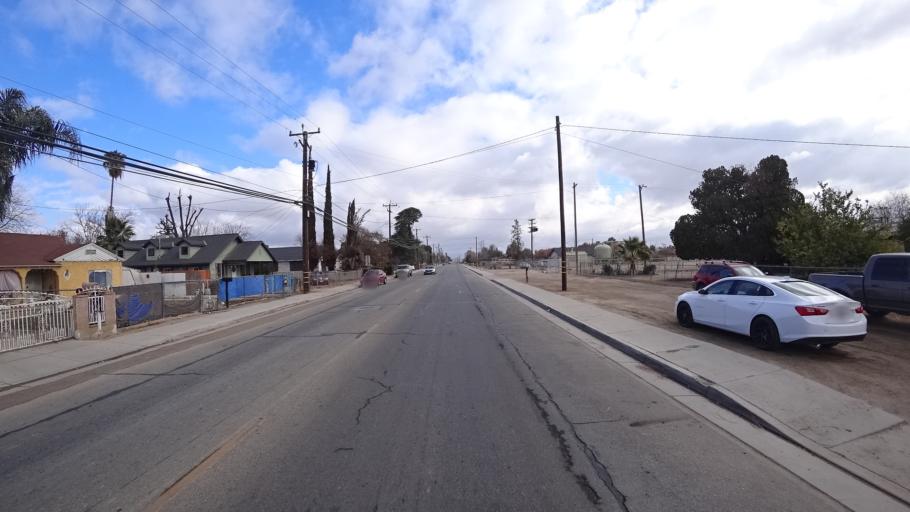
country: US
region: California
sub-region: Kern County
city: Bakersfield
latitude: 35.3395
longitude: -118.9930
